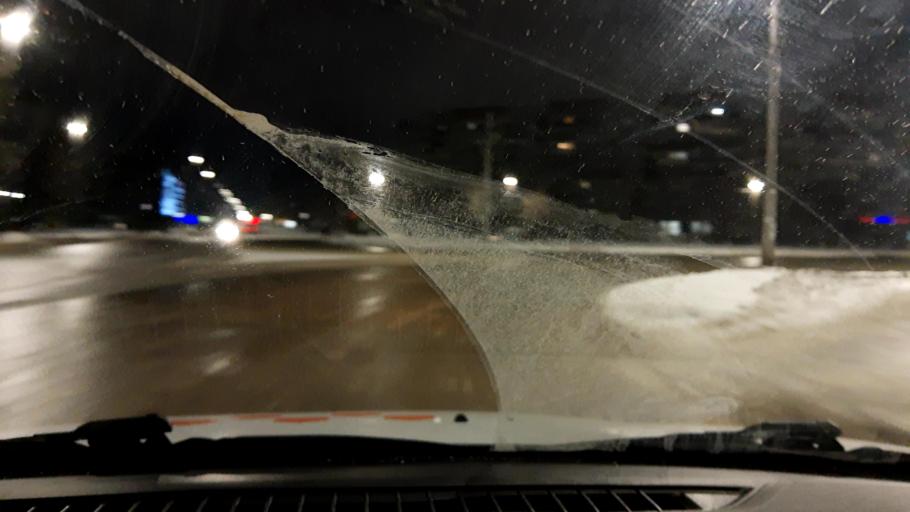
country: RU
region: Nizjnij Novgorod
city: Dzerzhinsk
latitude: 56.2305
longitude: 43.4572
